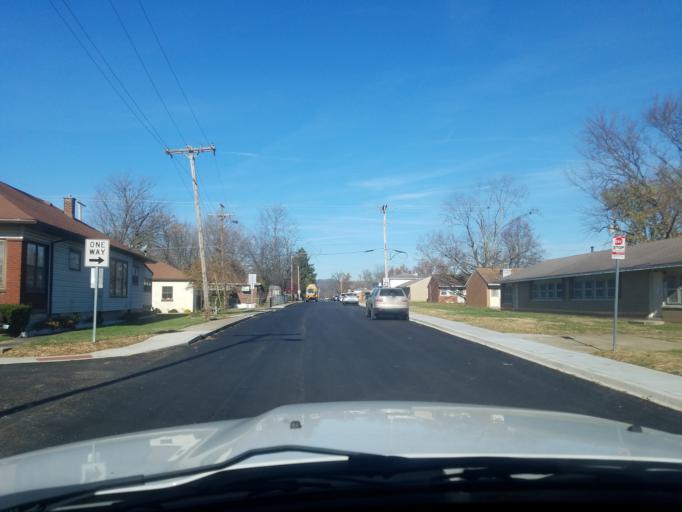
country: US
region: Indiana
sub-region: Floyd County
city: New Albany
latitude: 38.2988
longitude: -85.8285
